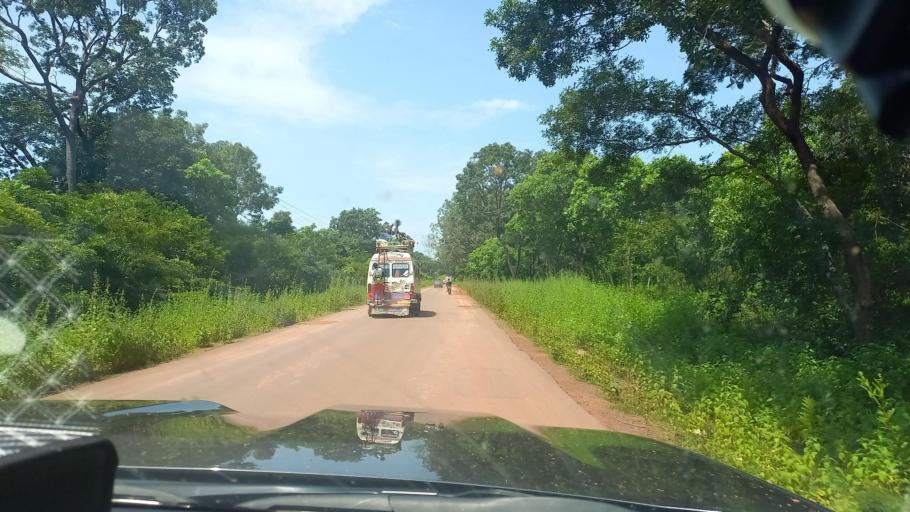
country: SN
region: Ziguinchor
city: Bignona
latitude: 12.8574
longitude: -16.1067
